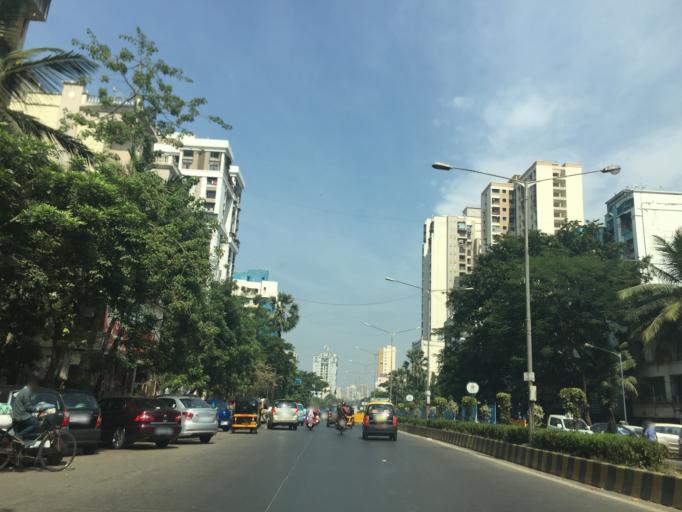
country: IN
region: Maharashtra
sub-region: Mumbai Suburban
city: Borivli
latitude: 19.2218
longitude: 72.8408
